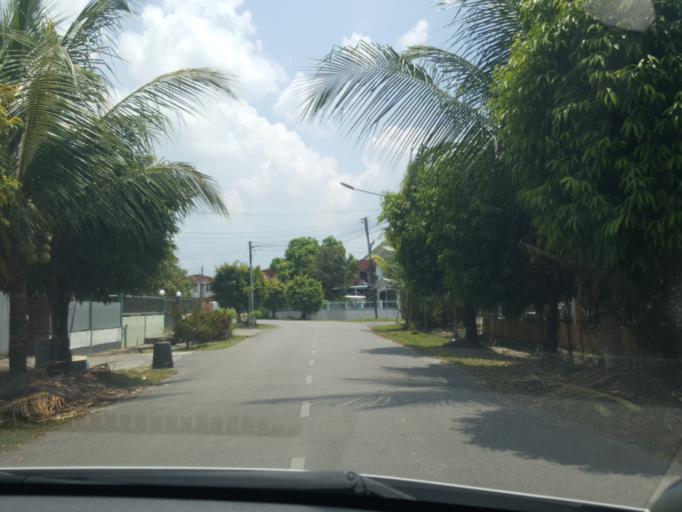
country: MY
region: Sarawak
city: Sarikei
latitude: 2.1219
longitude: 111.5253
